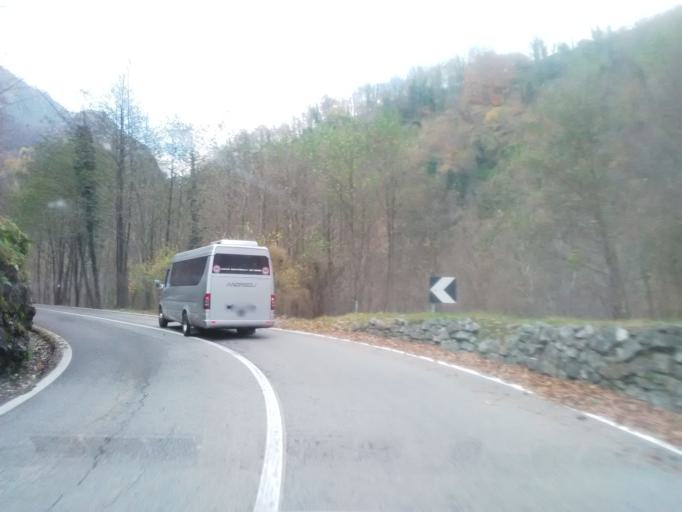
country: IT
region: Piedmont
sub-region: Provincia di Vercelli
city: Sabbia
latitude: 45.8417
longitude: 8.2540
